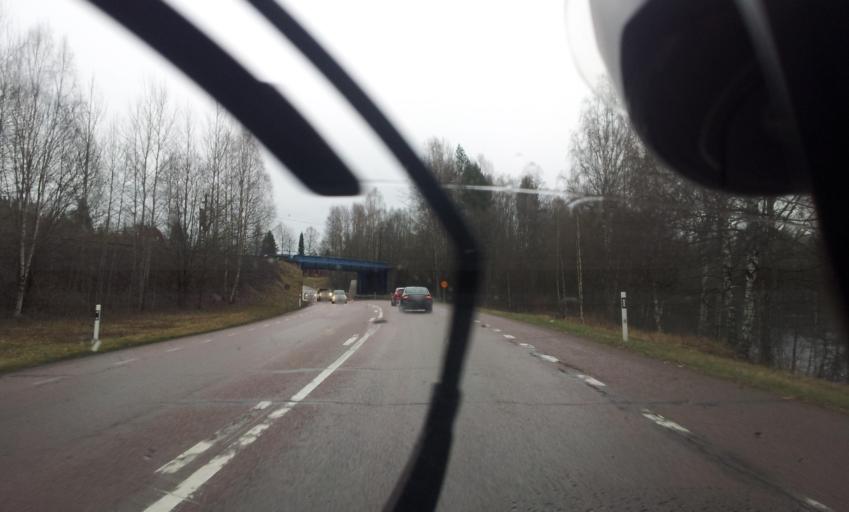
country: SE
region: Dalarna
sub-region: Gagnefs Kommun
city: Djuras
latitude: 60.5422
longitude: 15.2804
